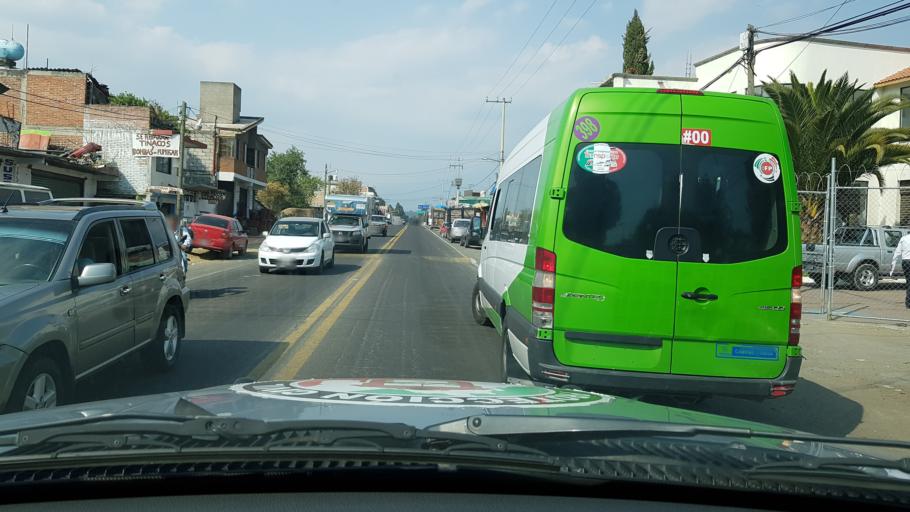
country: MX
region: Mexico
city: Tepetlixpa
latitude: 19.0294
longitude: -98.8142
